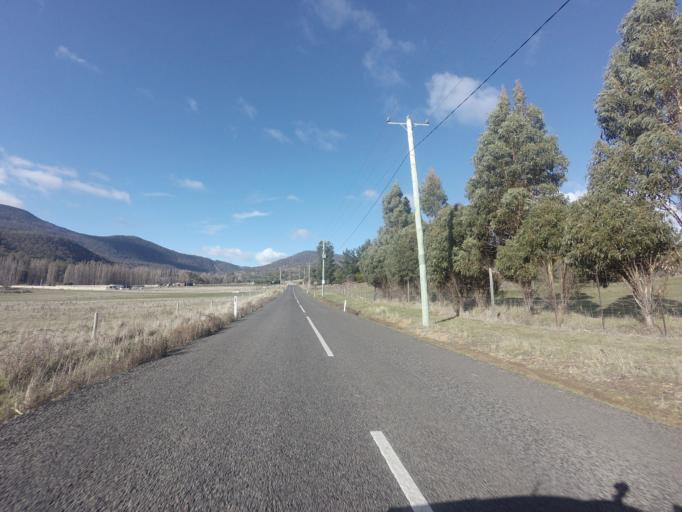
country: AU
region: Tasmania
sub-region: Derwent Valley
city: New Norfolk
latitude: -42.7974
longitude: 147.1322
